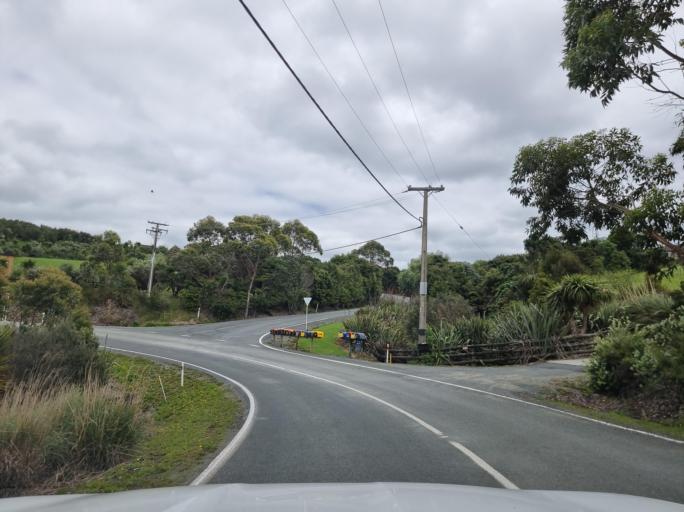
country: NZ
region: Auckland
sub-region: Auckland
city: Wellsford
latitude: -36.0909
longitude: 174.5308
